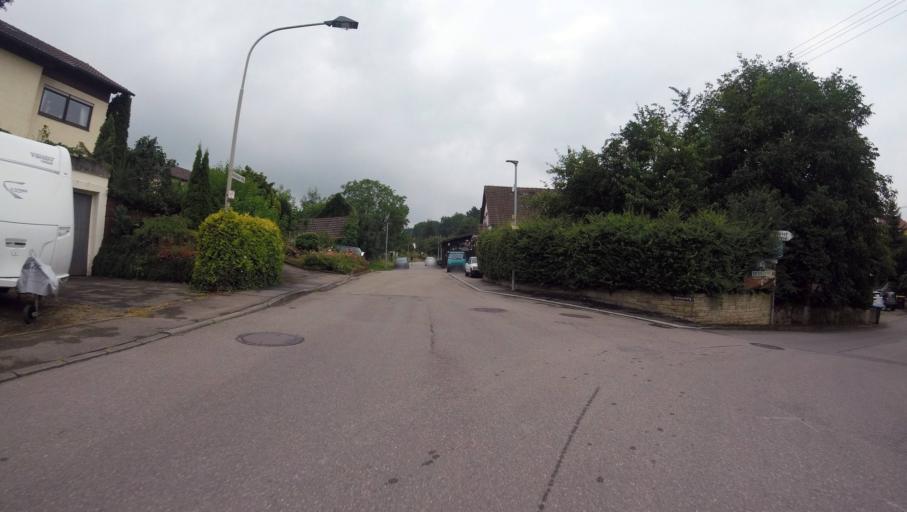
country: DE
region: Baden-Wuerttemberg
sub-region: Regierungsbezirk Stuttgart
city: Oppenweiler
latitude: 48.9851
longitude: 9.4549
